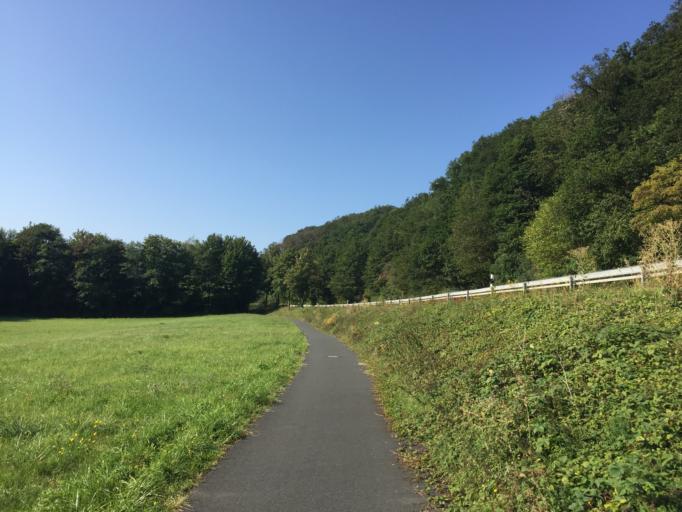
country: DE
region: Hesse
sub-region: Regierungsbezirk Giessen
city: Schoeffengrund
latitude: 50.4553
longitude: 8.5601
